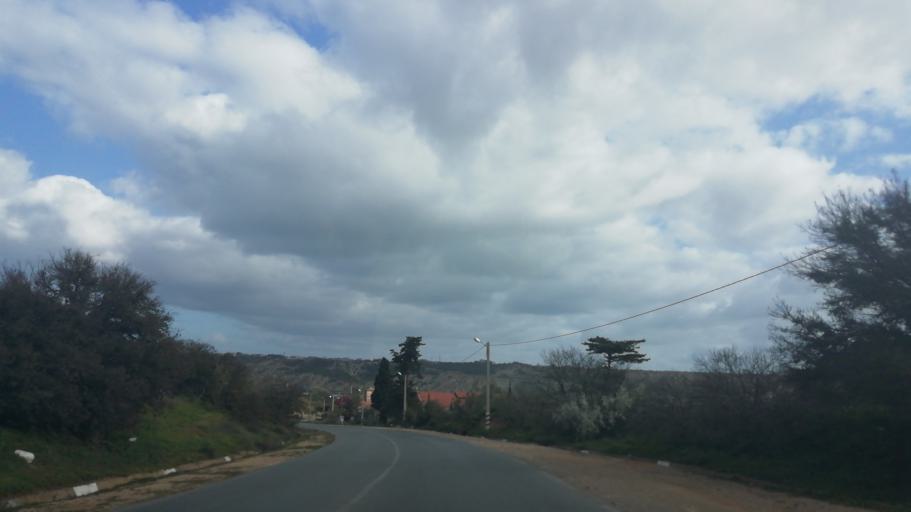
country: DZ
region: Relizane
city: Mazouna
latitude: 36.2962
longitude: 0.6576
